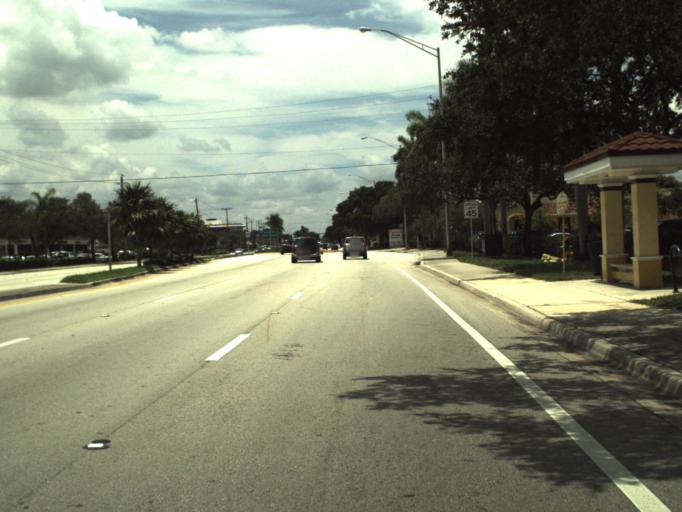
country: US
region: Florida
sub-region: Broward County
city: Margate
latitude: 26.2355
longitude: -80.1992
